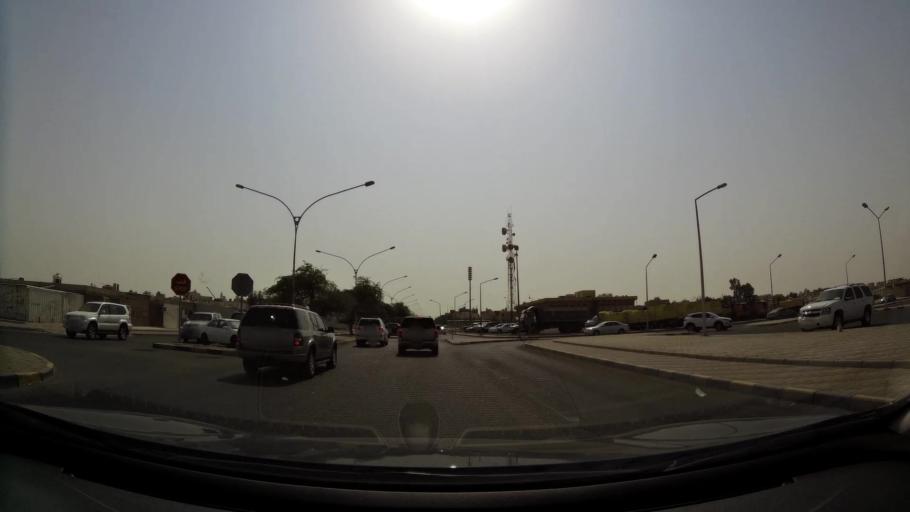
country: KW
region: Muhafazat al Jahra'
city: Al Jahra'
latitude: 29.3269
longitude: 47.6809
